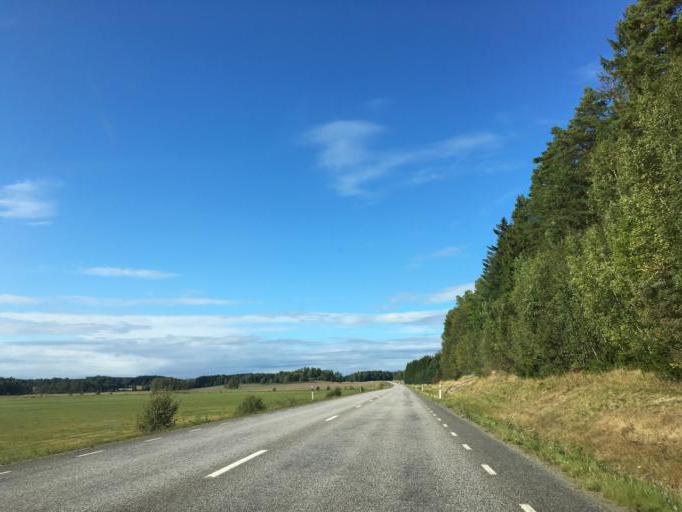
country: SE
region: Soedermanland
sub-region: Nykopings Kommun
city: Nykoping
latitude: 58.7923
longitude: 16.9556
